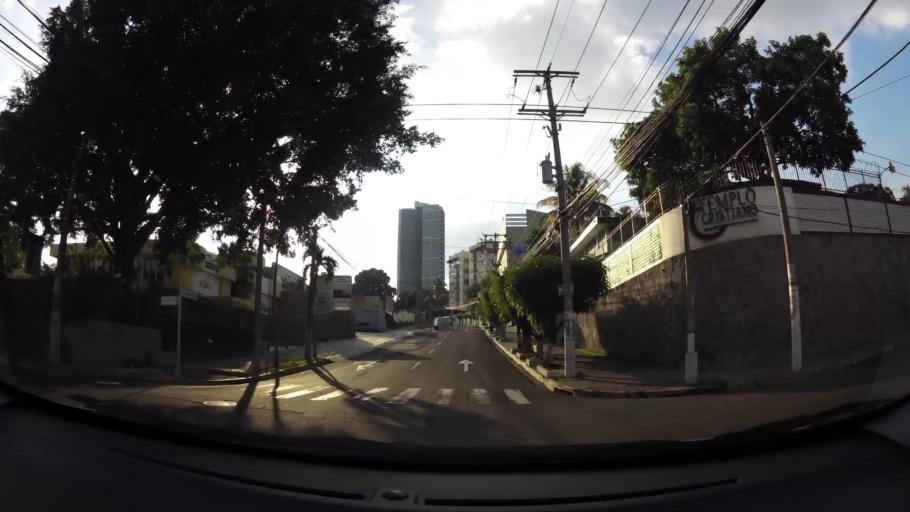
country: SV
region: La Libertad
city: Antiguo Cuscatlan
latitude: 13.6953
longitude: -89.2341
